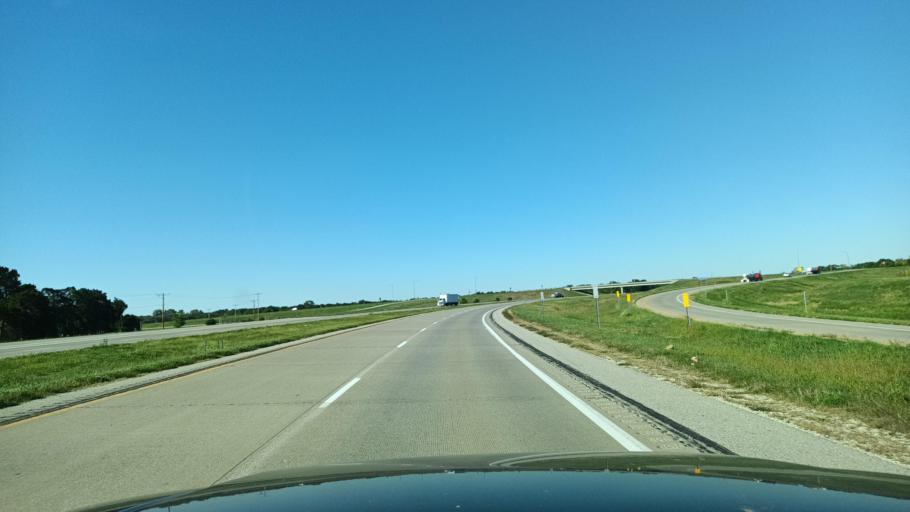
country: US
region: Iowa
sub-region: Lee County
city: Fort Madison
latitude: 40.6719
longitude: -91.2662
